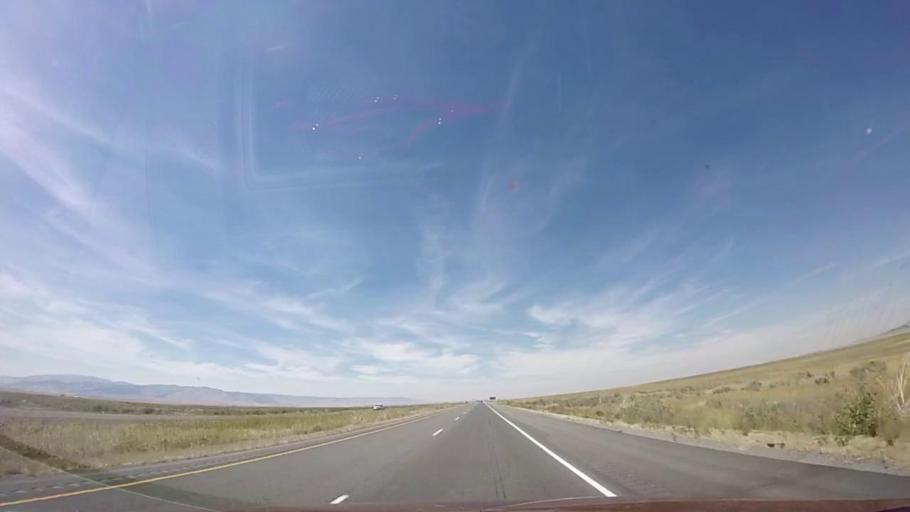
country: US
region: Idaho
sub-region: Power County
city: American Falls
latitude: 42.3027
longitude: -113.1814
